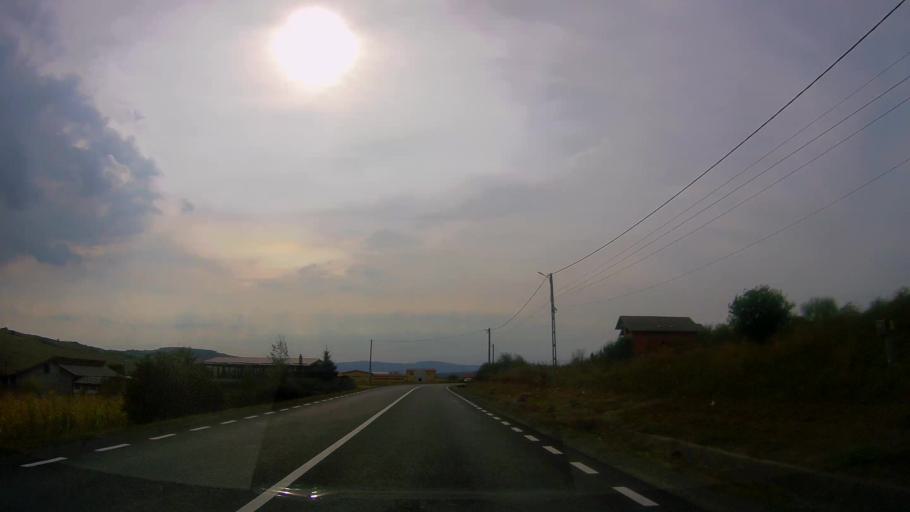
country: RO
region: Salaj
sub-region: Comuna Hereclean
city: Hereclean
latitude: 47.2525
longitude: 22.9818
